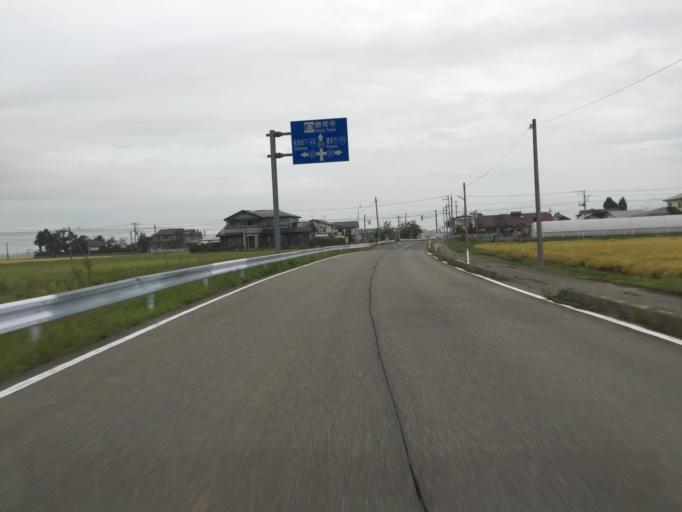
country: JP
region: Fukushima
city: Kitakata
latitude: 37.5532
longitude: 139.8722
